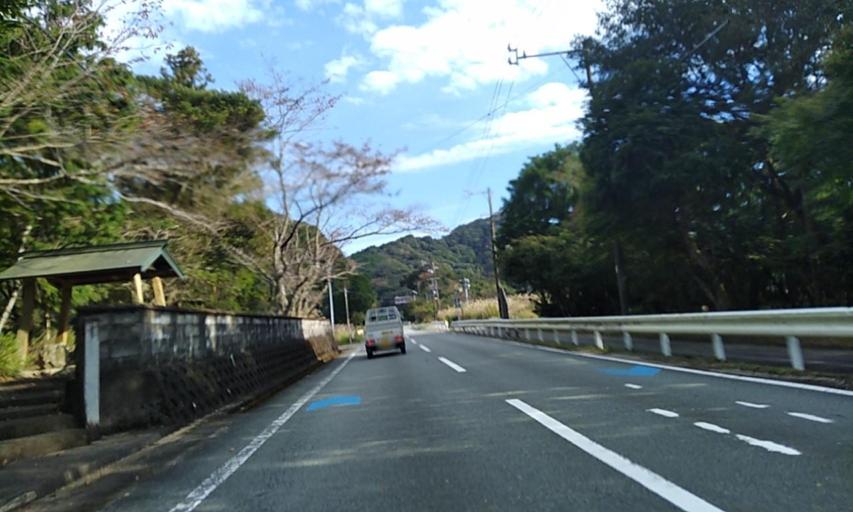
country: JP
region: Mie
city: Ise
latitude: 34.2976
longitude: 136.5923
